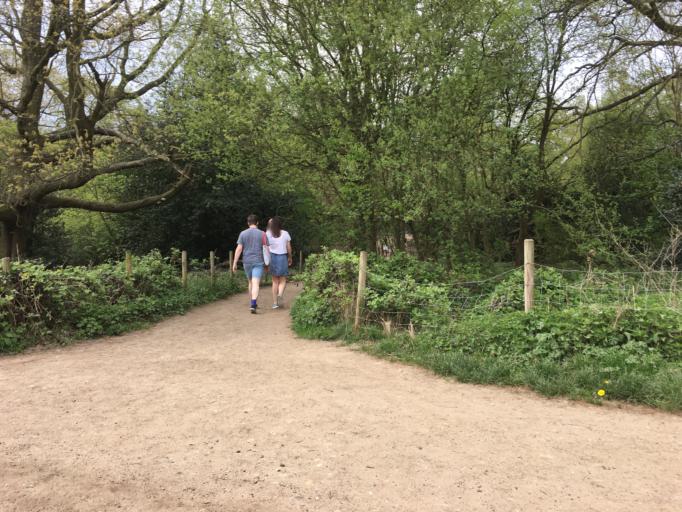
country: GB
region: England
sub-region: Greater London
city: Belsize Park
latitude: 51.5639
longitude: -0.1666
